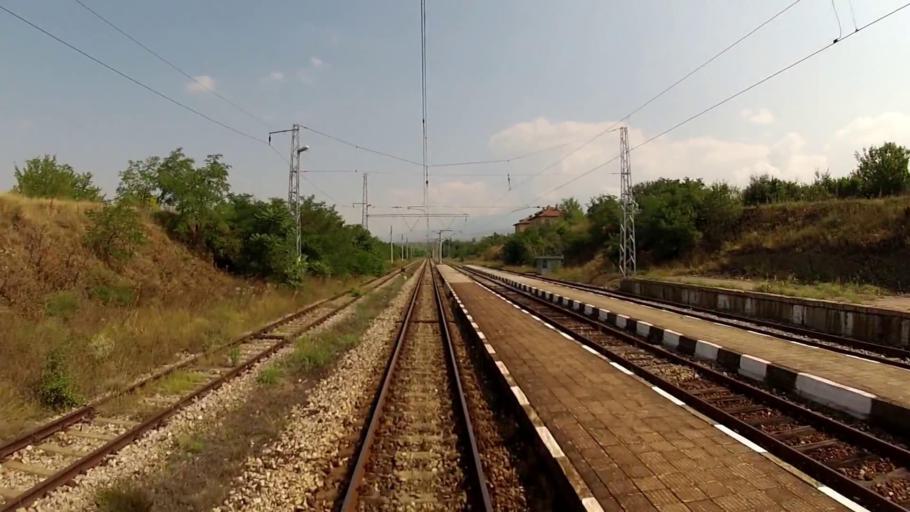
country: BG
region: Blagoevgrad
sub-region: Obshtina Sandanski
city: Sandanski
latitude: 41.5434
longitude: 23.2516
